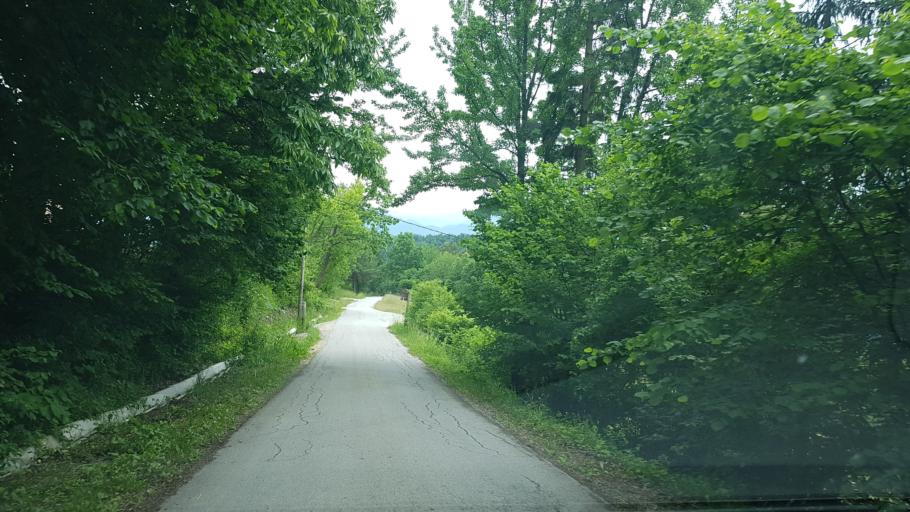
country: SI
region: Dobrna
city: Dobrna
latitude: 46.3603
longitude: 15.2418
